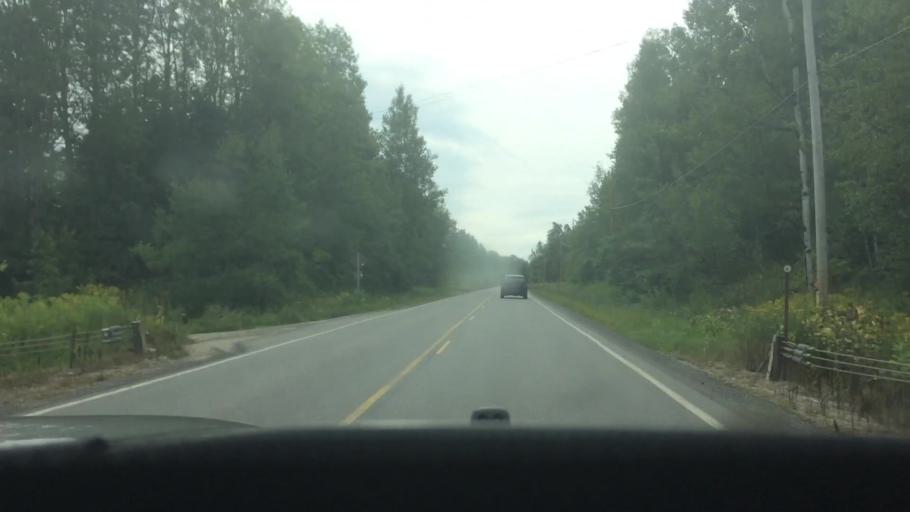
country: US
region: New York
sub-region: St. Lawrence County
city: Canton
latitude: 44.4835
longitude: -75.2471
